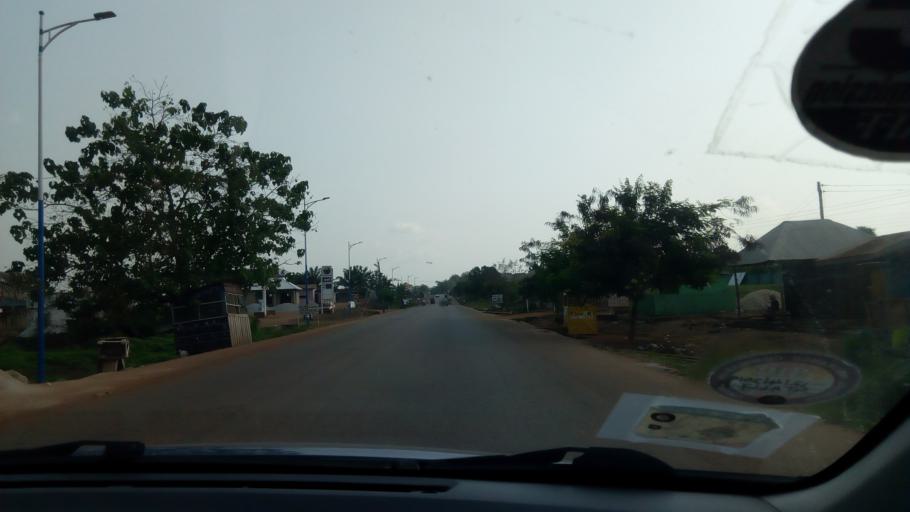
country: GH
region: Western
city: Bibiani
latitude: 6.7924
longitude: -2.5167
